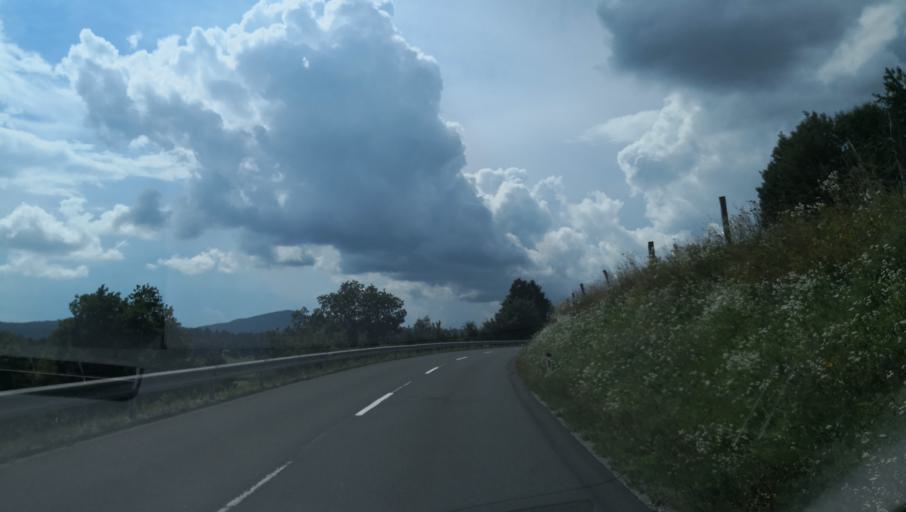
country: SI
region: Zuzemberk
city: Zuzemberk
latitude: 45.8542
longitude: 14.8868
